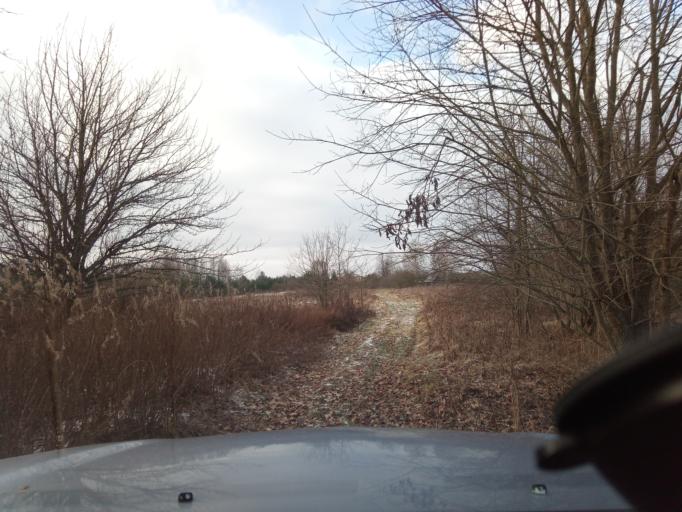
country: LT
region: Alytaus apskritis
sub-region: Alytaus rajonas
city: Daugai
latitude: 54.1159
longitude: 24.2337
